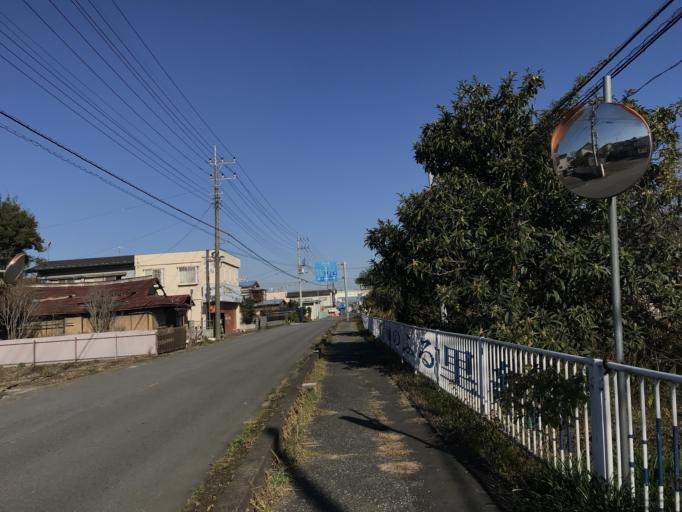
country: JP
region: Ibaraki
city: Yuki
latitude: 36.2954
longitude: 139.8659
